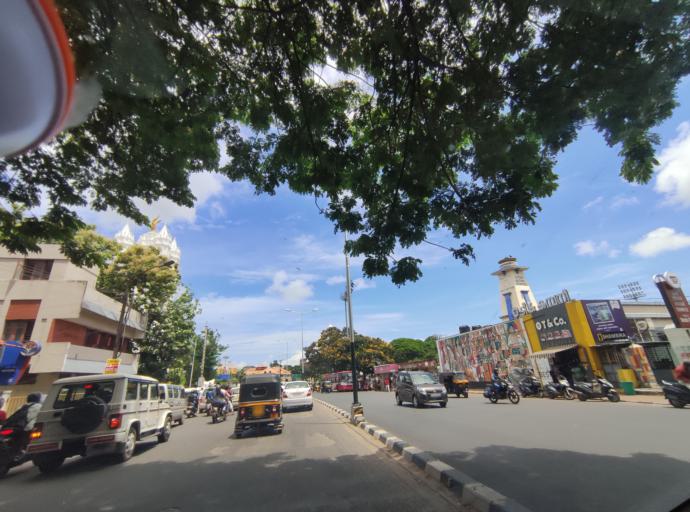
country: IN
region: Kerala
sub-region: Thiruvananthapuram
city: Thiruvananthapuram
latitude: 8.5049
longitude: 76.9514
